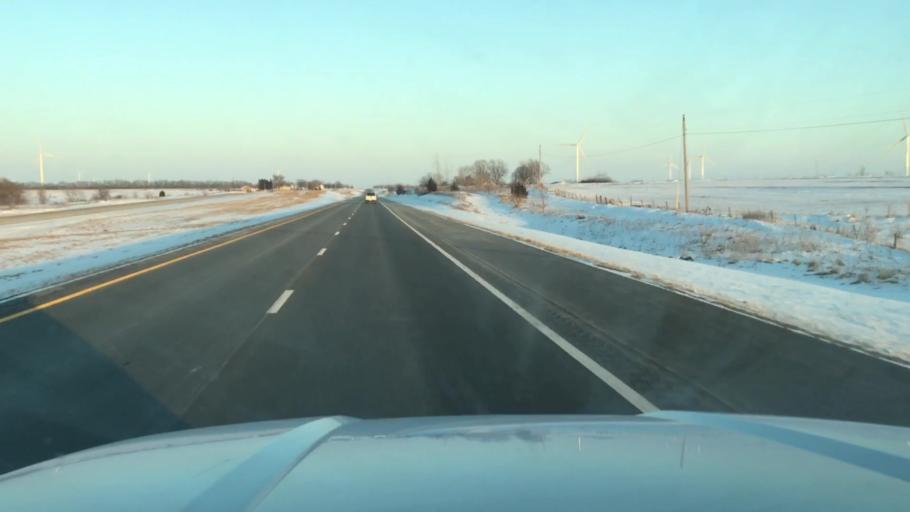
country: US
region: Missouri
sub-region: DeKalb County
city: Maysville
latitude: 39.7616
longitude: -94.4275
